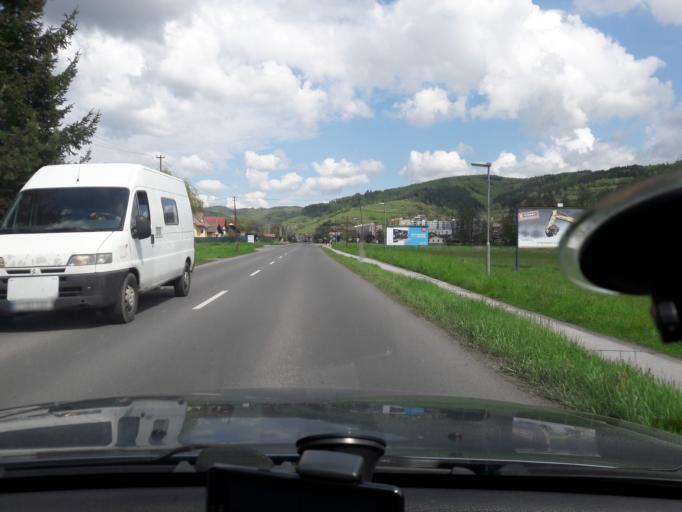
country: SK
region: Banskobystricky
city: Hrinova
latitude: 48.5723
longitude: 19.5152
